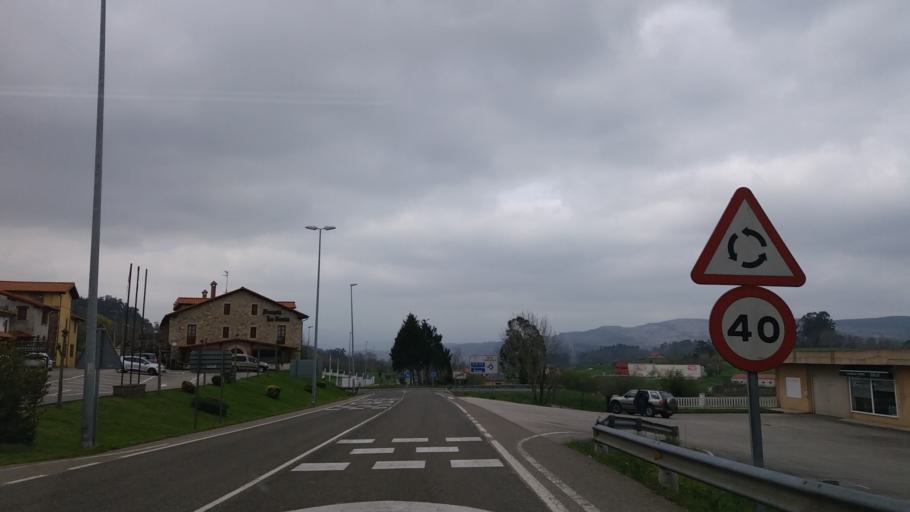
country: ES
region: Cantabria
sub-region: Provincia de Cantabria
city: Reocin
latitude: 43.3494
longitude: -4.1347
